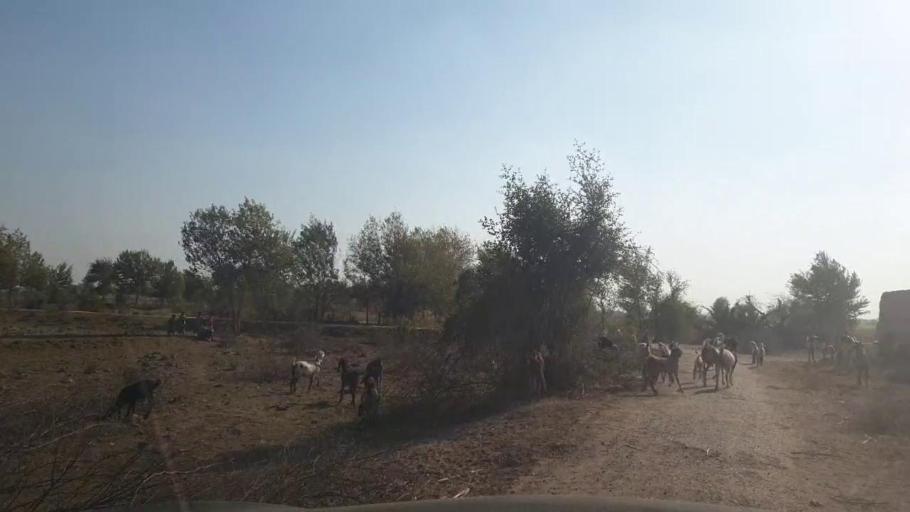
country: PK
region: Sindh
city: Mirpur Mathelo
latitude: 27.9956
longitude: 69.4841
